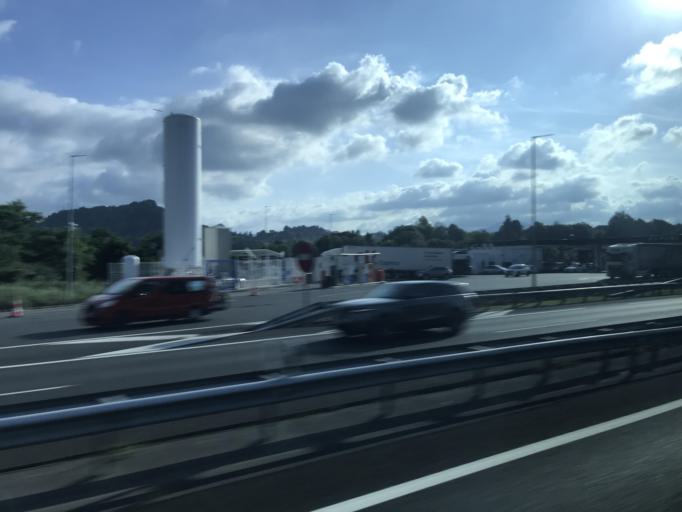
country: ES
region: Basque Country
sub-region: Provincia de Guipuzcoa
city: Hernani
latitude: 43.2783
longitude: -1.9775
